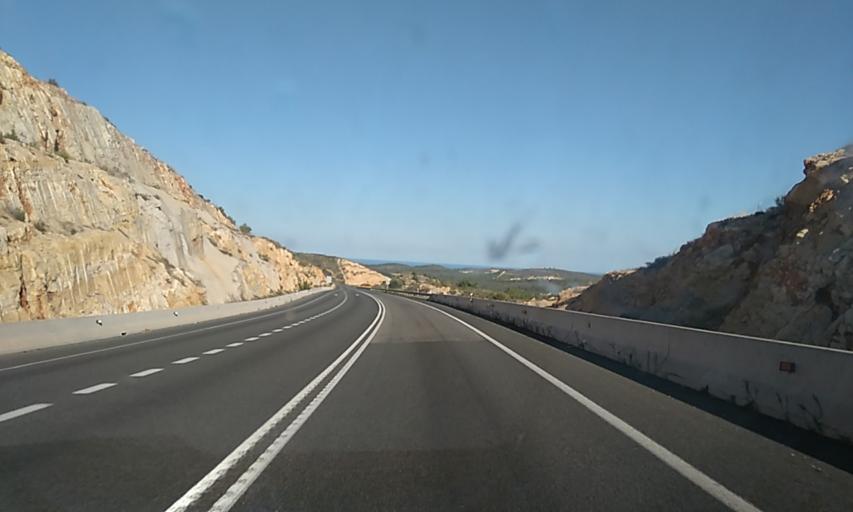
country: ES
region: Valencia
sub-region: Provincia de Castello
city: Torreblanca
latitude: 40.2105
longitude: 0.1183
